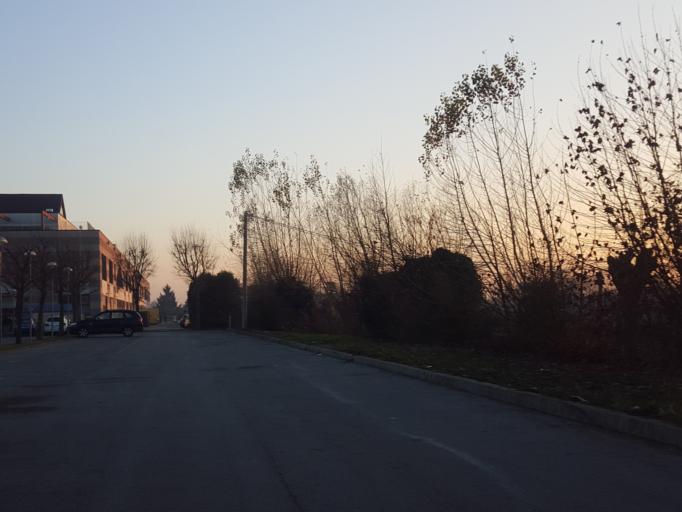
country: IT
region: Veneto
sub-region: Provincia di Vicenza
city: Bolzano Vicentino
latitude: 45.5885
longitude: 11.6226
